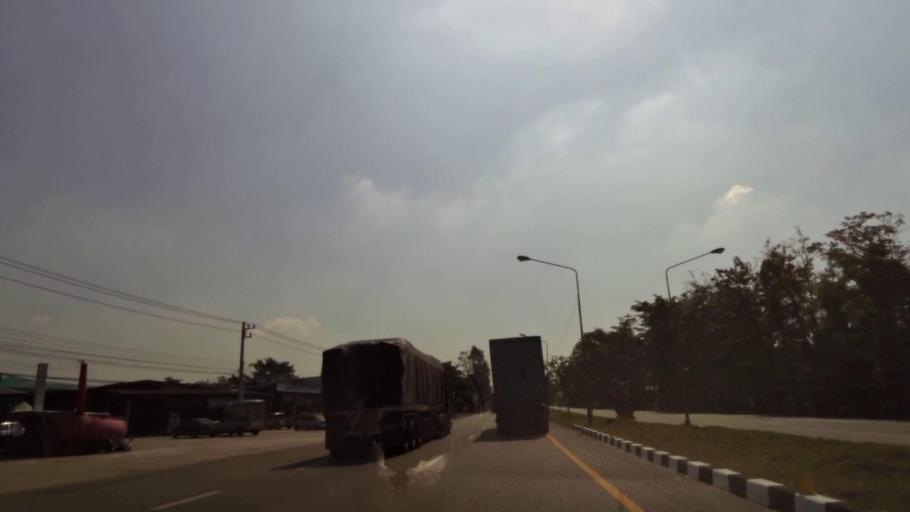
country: TH
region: Phichit
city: Bueng Na Rang
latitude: 16.1389
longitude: 100.1257
